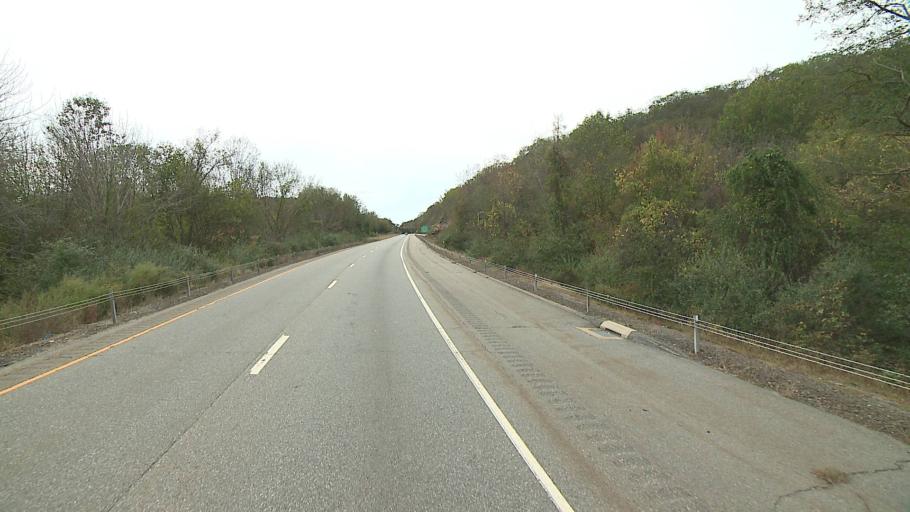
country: US
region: Connecticut
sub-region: Middlesex County
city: Chester Center
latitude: 41.4009
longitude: -72.4733
